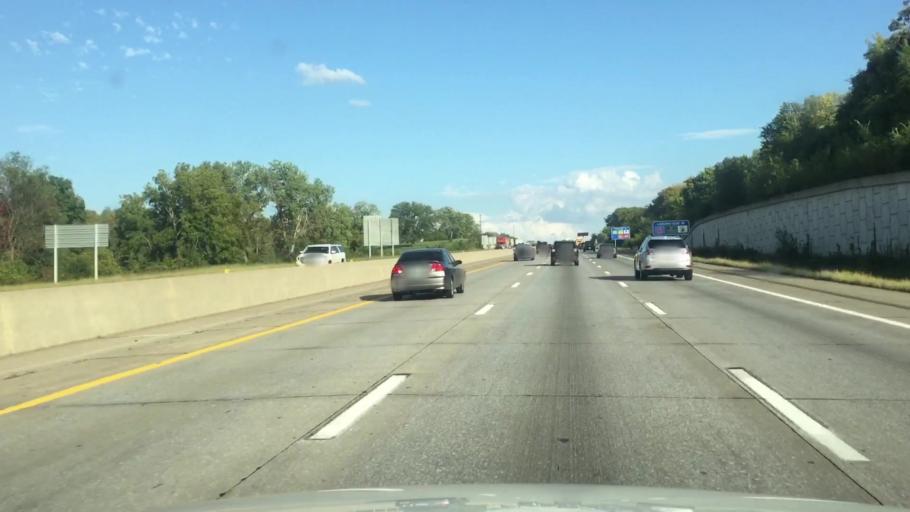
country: US
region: Missouri
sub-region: Jackson County
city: Blue Springs
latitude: 39.0366
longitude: -94.3246
